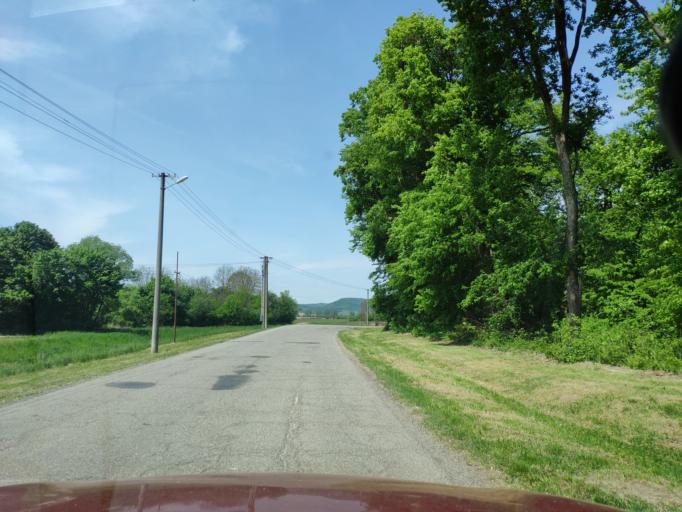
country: SK
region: Banskobystricky
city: Rimavska Sobota
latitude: 48.4483
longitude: 20.1132
